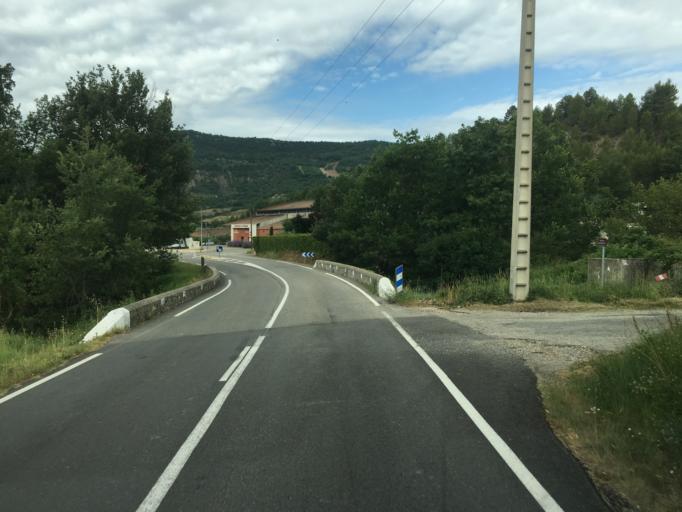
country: FR
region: Rhone-Alpes
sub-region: Departement de la Drome
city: Nyons
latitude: 44.3918
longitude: 5.2057
